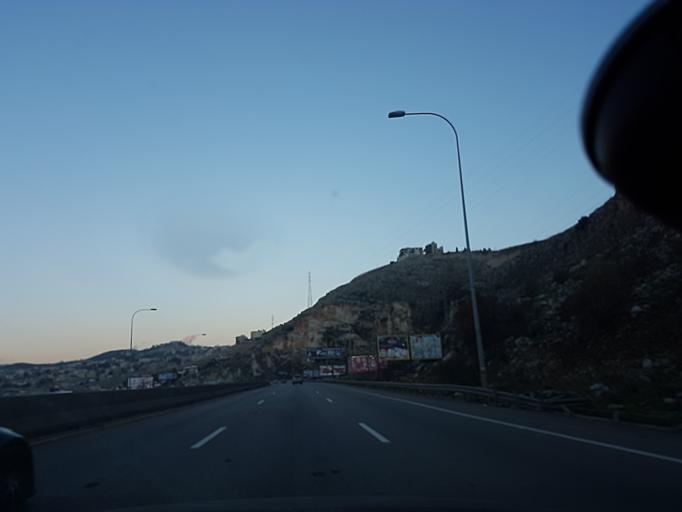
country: LB
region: Liban-Sud
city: Sidon
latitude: 33.6499
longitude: 35.4139
